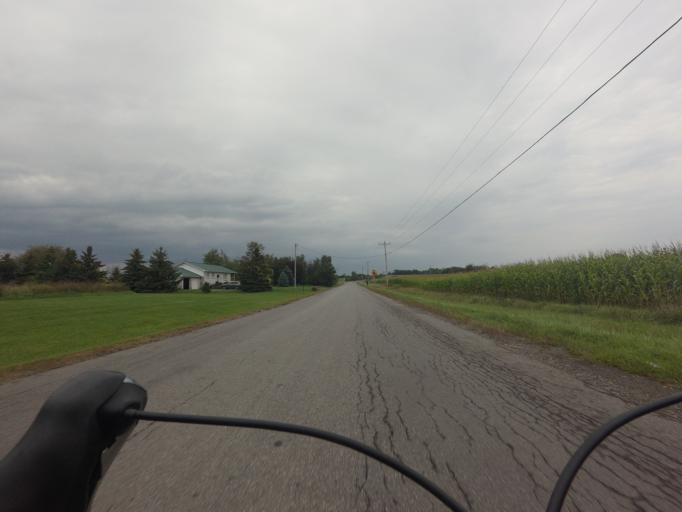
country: CA
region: Ontario
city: Bells Corners
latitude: 45.1429
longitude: -75.7674
